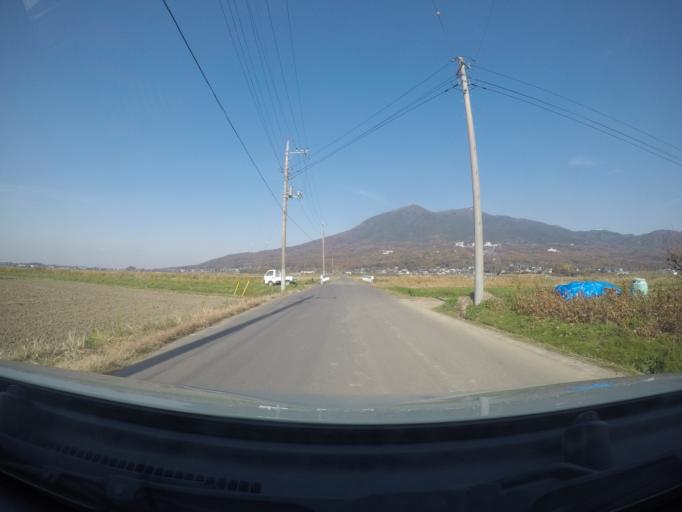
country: JP
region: Ibaraki
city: Tsukuba
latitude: 36.1953
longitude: 140.0895
